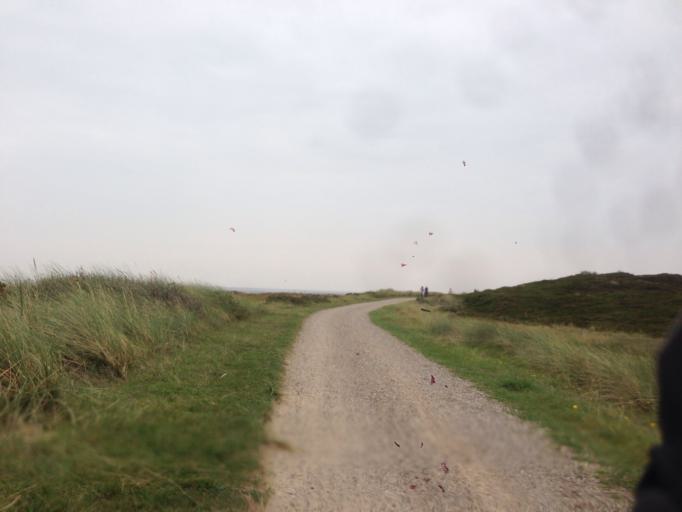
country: DE
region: Schleswig-Holstein
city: Westerland
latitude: 54.8374
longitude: 8.2947
